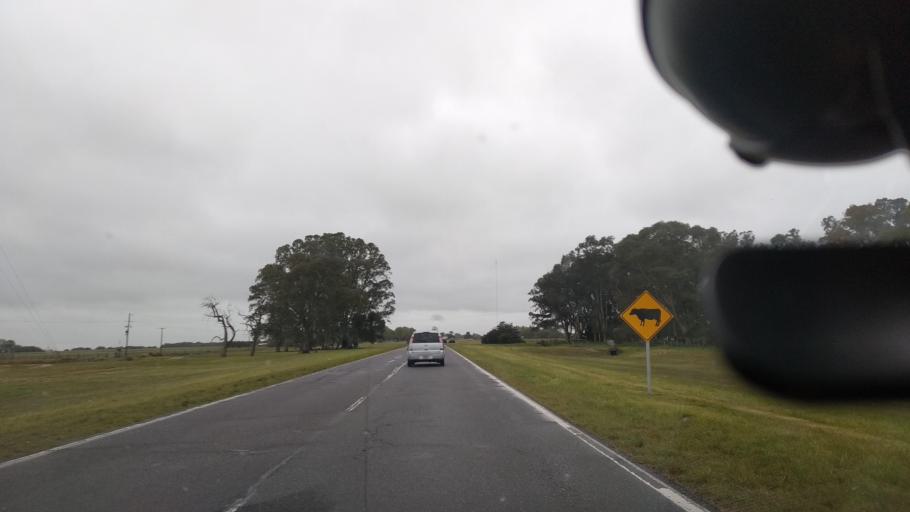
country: AR
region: Buenos Aires
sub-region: Partido de Castelli
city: Castelli
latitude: -35.9845
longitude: -57.4498
